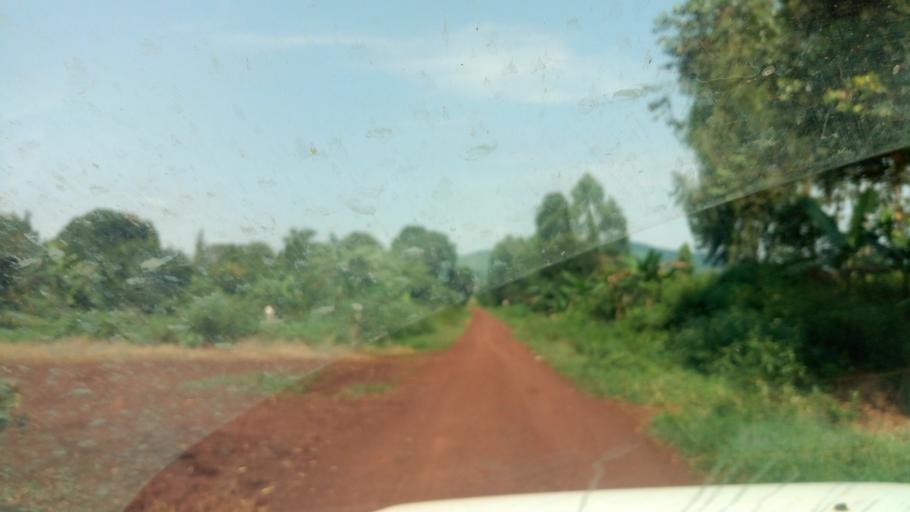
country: UG
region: Western Region
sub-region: Masindi District
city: Masindi
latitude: 1.6622
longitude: 31.8128
